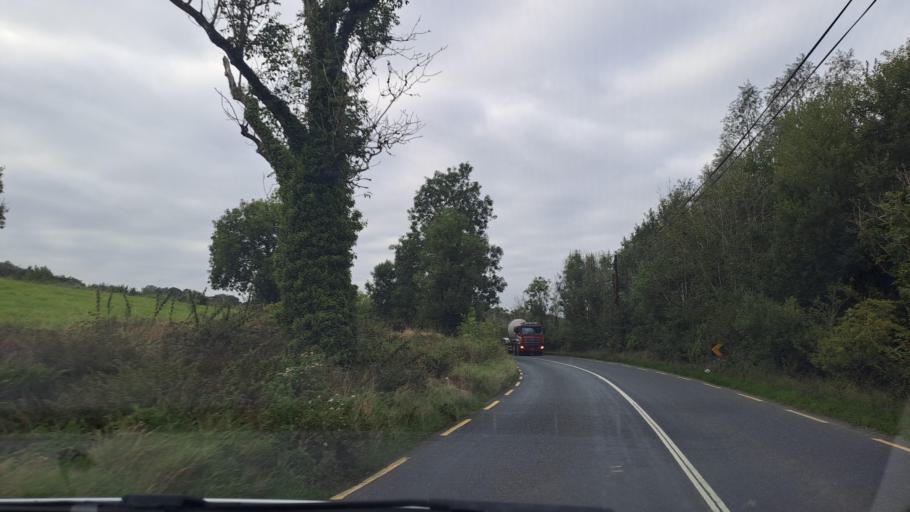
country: IE
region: Ulster
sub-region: County Monaghan
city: Carrickmacross
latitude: 54.0148
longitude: -6.7591
